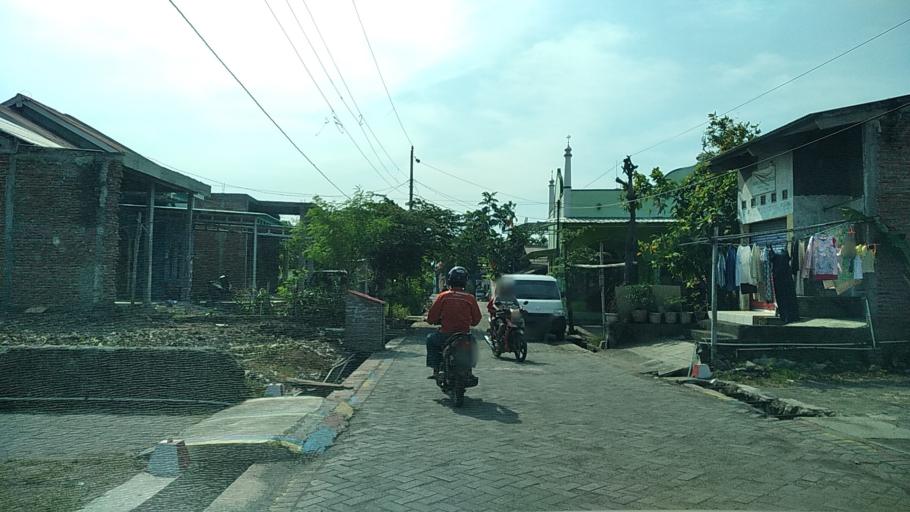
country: ID
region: Central Java
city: Semarang
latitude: -6.9682
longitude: 110.4528
